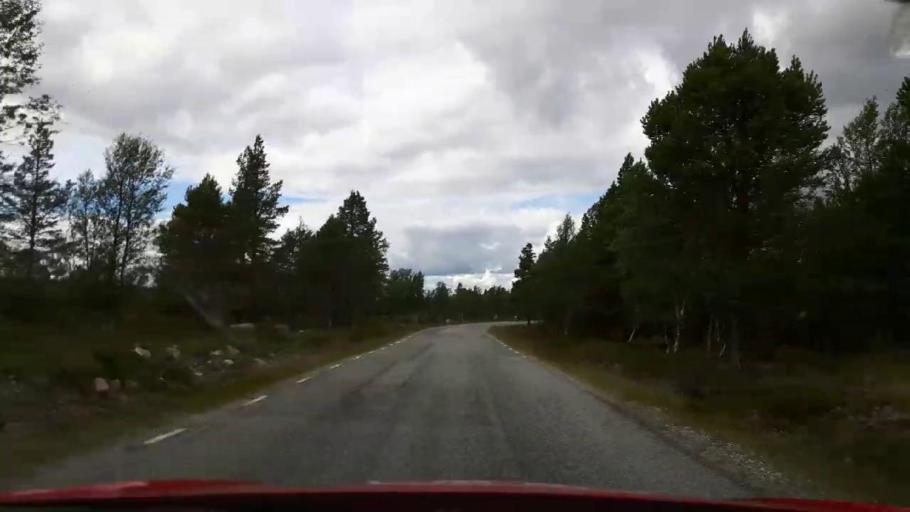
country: NO
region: Hedmark
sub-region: Engerdal
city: Engerdal
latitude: 62.2773
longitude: 12.8827
